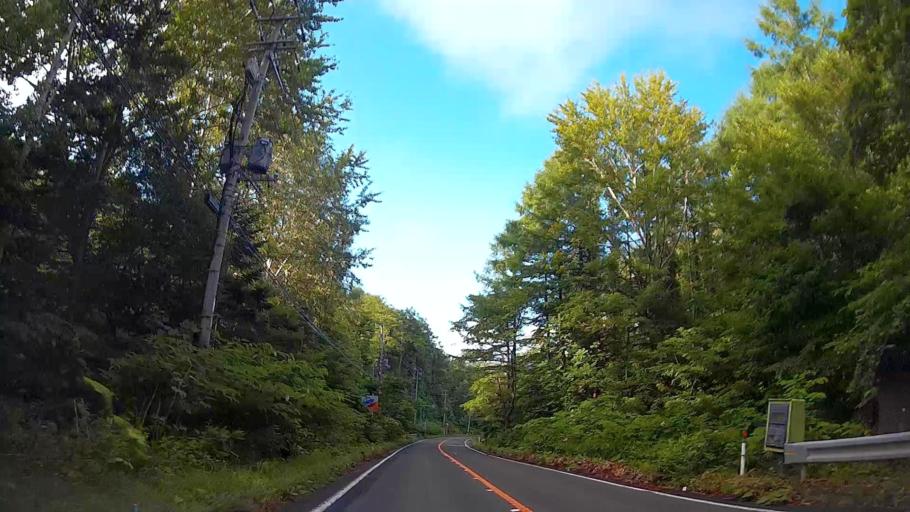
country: JP
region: Hokkaido
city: Date
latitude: 42.5466
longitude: 140.8569
